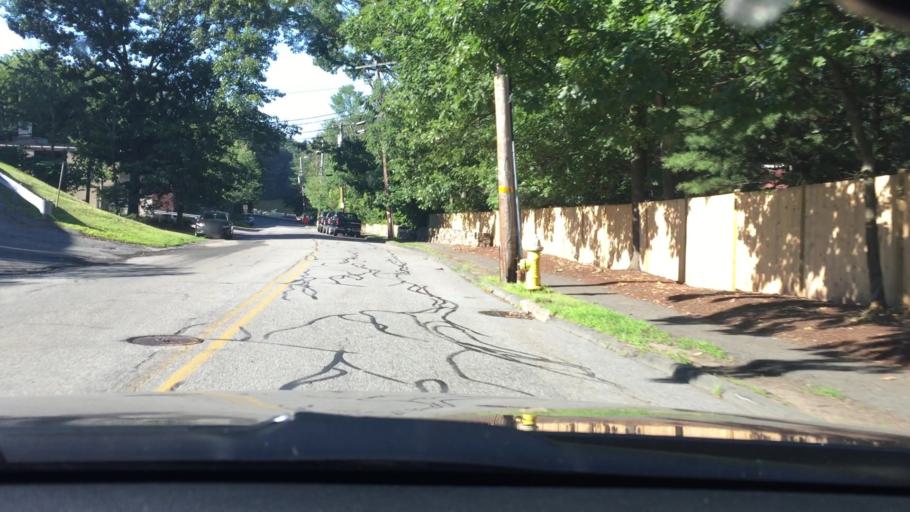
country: US
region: Massachusetts
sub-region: Norfolk County
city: Needham
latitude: 42.2904
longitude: -71.2378
